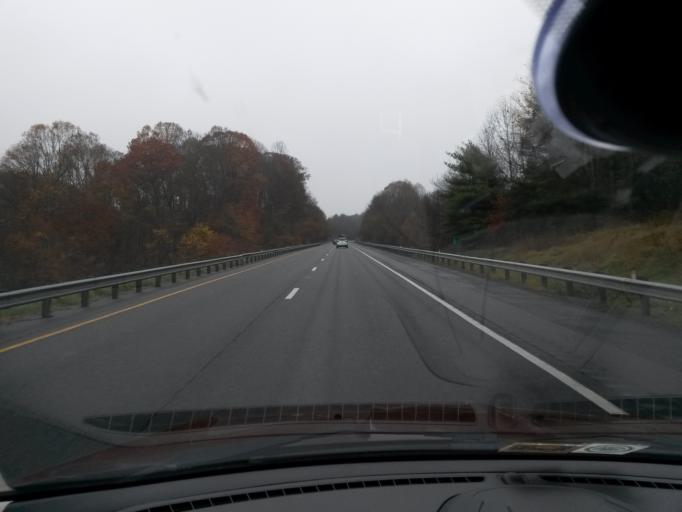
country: US
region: Virginia
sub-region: Carroll County
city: Woodlawn
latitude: 36.7574
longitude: -80.7870
